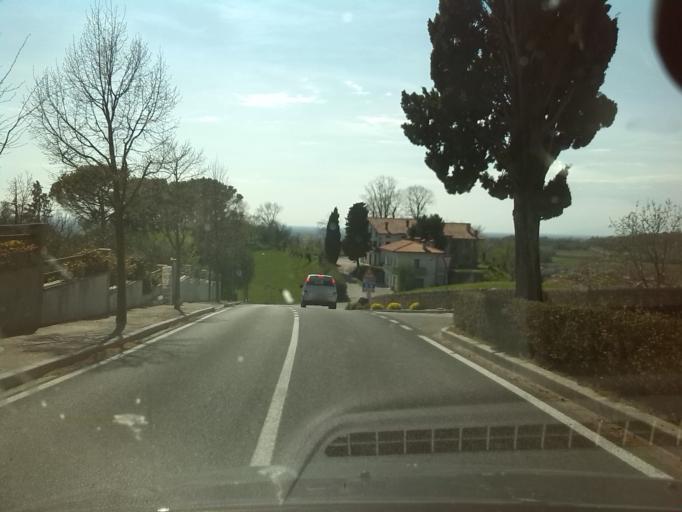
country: IT
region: Friuli Venezia Giulia
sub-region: Provincia di Udine
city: Moruzzo
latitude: 46.1191
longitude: 13.1222
